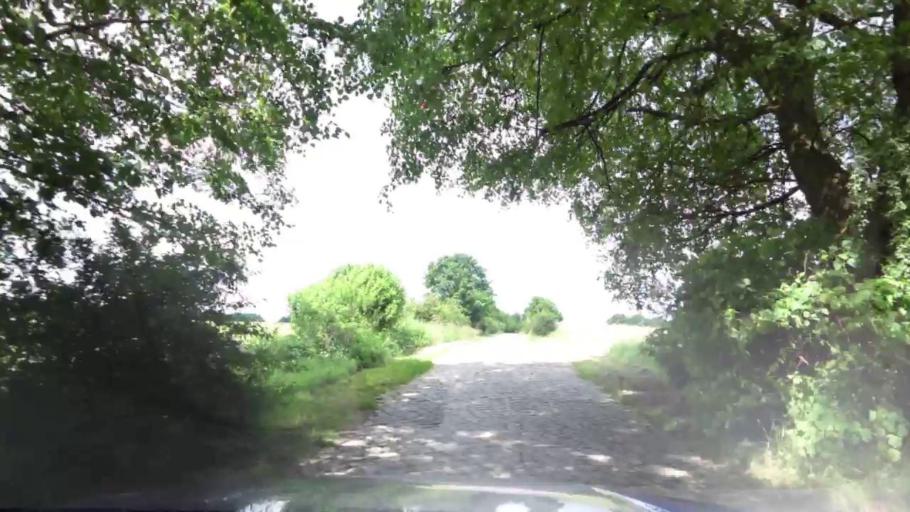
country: PL
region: West Pomeranian Voivodeship
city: Trzcinsko Zdroj
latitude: 52.9536
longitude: 14.7144
